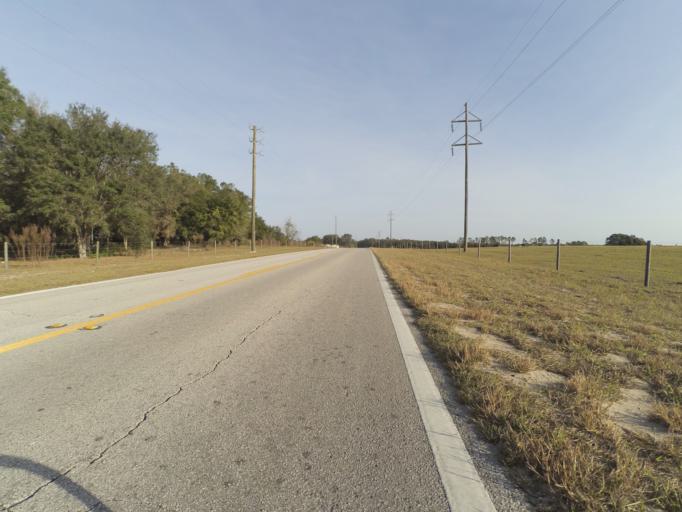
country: US
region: Florida
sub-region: Lake County
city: Umatilla
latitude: 28.9569
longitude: -81.6287
